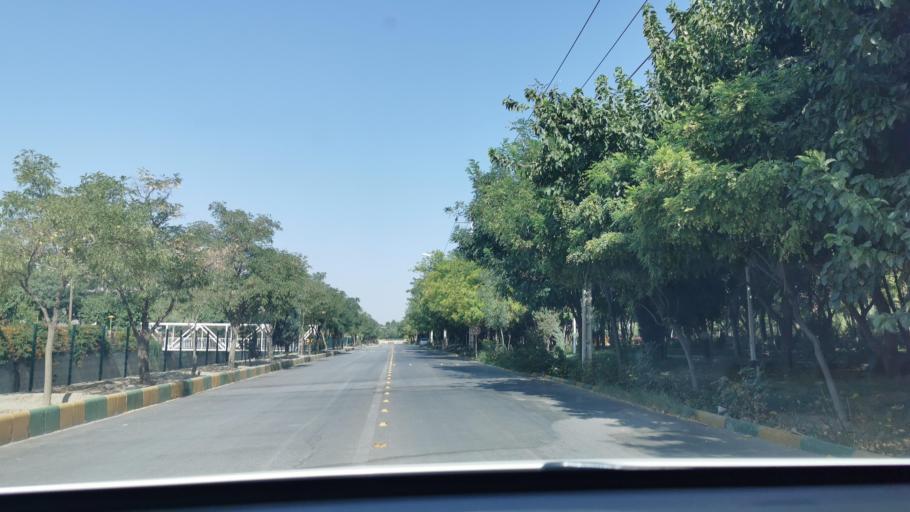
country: IR
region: Razavi Khorasan
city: Mashhad
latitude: 36.3301
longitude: 59.6343
